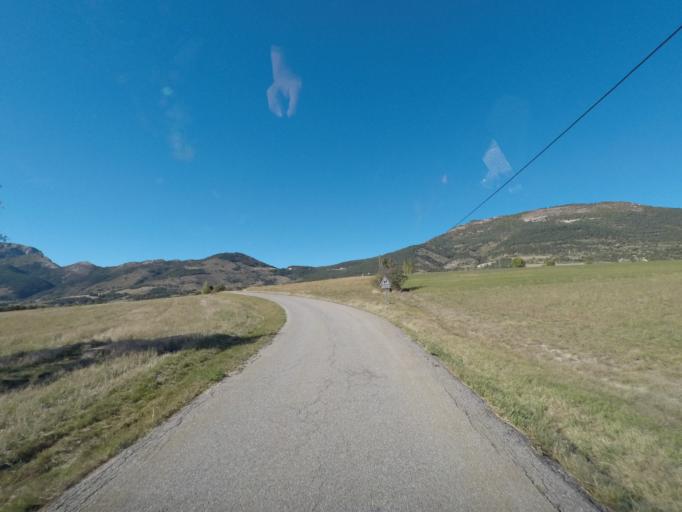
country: FR
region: Provence-Alpes-Cote d'Azur
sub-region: Departement des Hautes-Alpes
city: Serres
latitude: 44.4172
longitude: 5.5844
